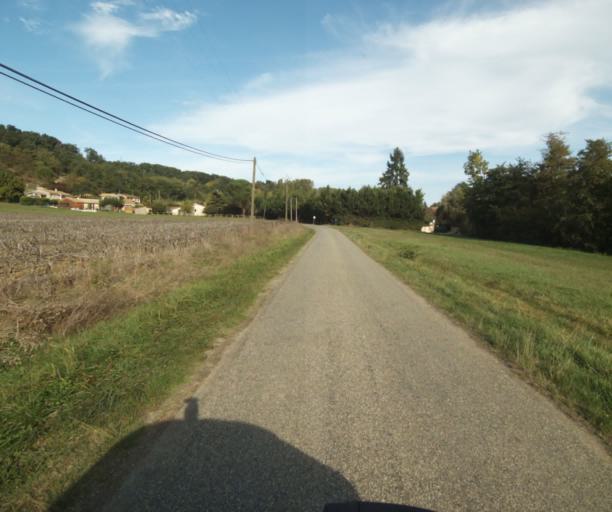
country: FR
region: Midi-Pyrenees
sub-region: Departement du Tarn-et-Garonne
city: Saint-Porquier
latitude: 43.9409
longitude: 1.1558
